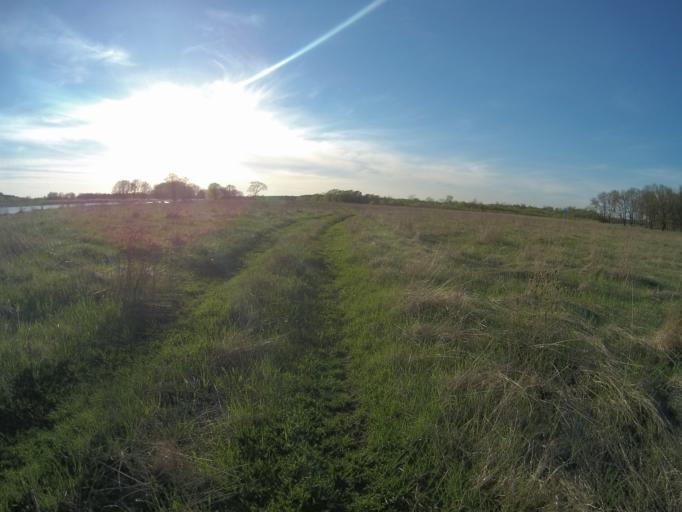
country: RU
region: Vladimir
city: Raduzhnyy
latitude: 56.0316
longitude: 40.2796
